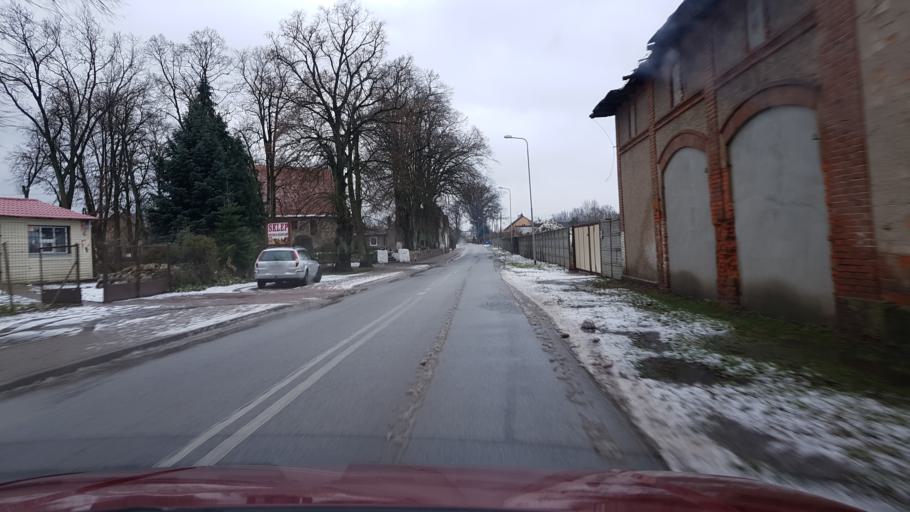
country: PL
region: West Pomeranian Voivodeship
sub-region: Powiat gryficki
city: Ploty
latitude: 53.7054
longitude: 15.2732
